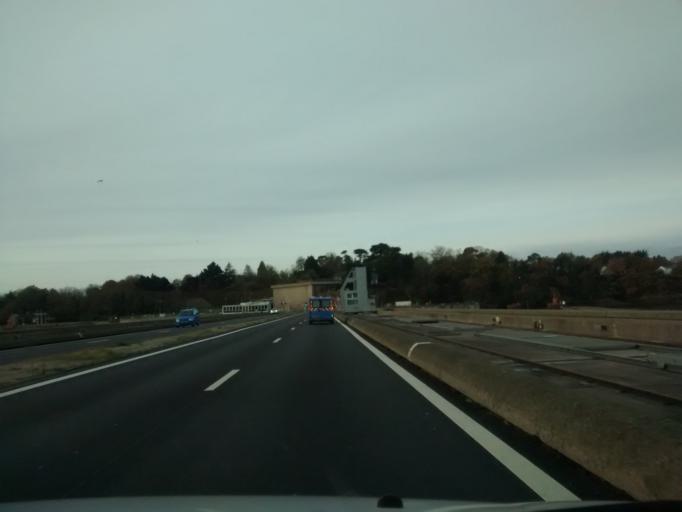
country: FR
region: Brittany
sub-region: Departement d'Ille-et-Vilaine
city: La Richardais
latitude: 48.6180
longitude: -2.0245
